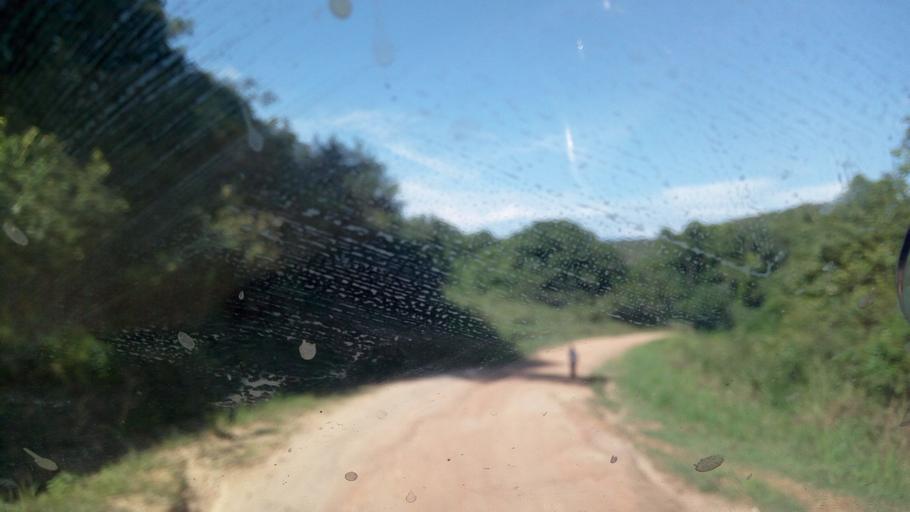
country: BI
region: Bururi
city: Rumonge
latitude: -4.3810
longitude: 28.8890
